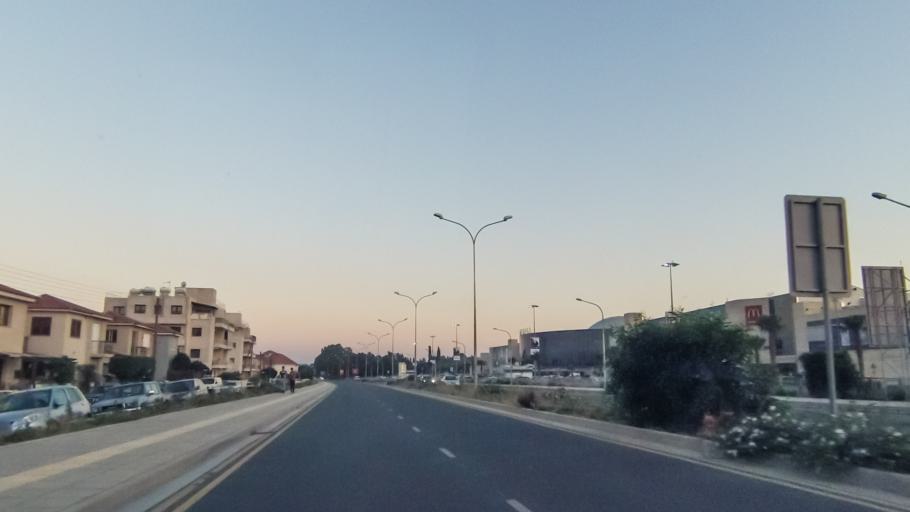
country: CY
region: Limassol
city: Ypsonas
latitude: 34.6551
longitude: 32.9975
